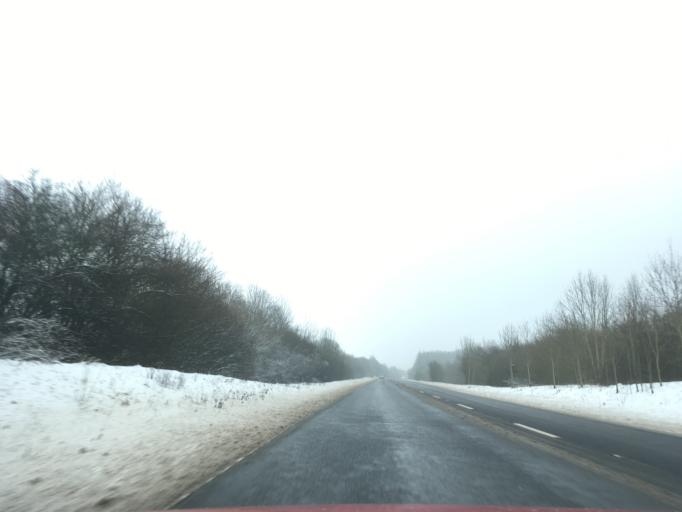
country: GB
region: England
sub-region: Warwickshire
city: Alcester
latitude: 52.2087
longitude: -1.8501
